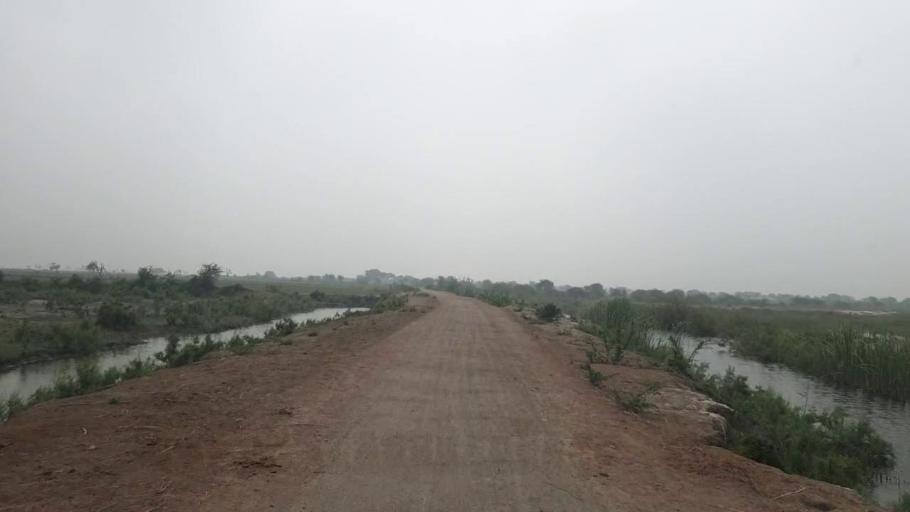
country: PK
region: Sindh
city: Badin
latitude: 24.5773
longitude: 68.6846
